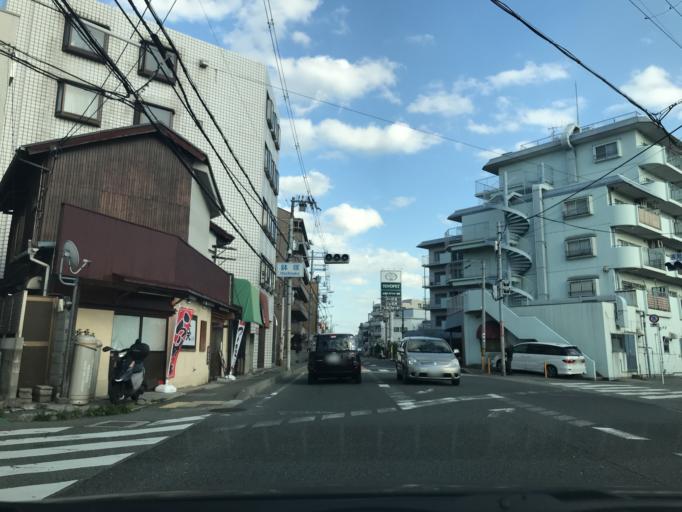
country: JP
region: Osaka
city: Ikeda
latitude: 34.8147
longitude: 135.4385
